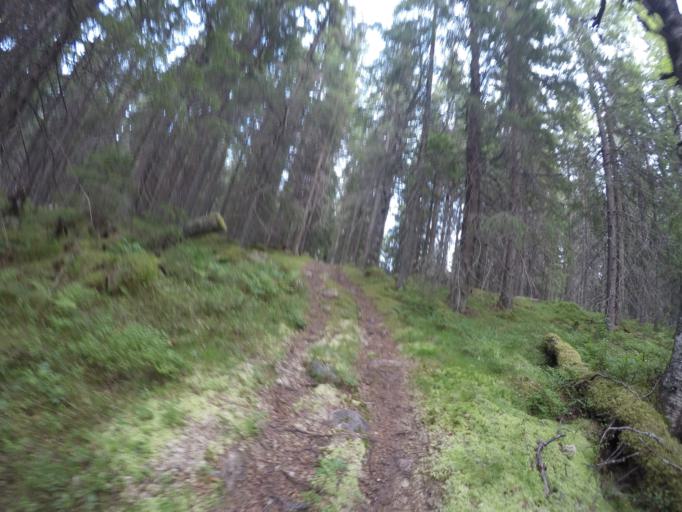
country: SE
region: Vaermland
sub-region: Filipstads Kommun
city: Lesjofors
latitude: 60.2038
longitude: 14.2898
